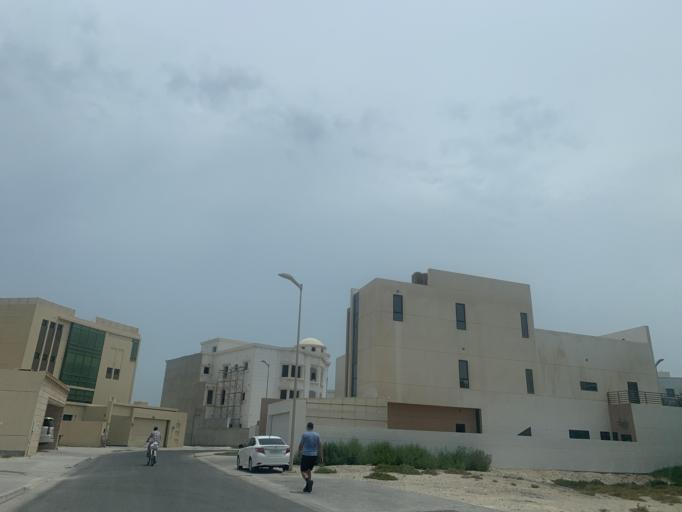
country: BH
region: Muharraq
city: Al Hadd
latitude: 26.2999
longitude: 50.6658
